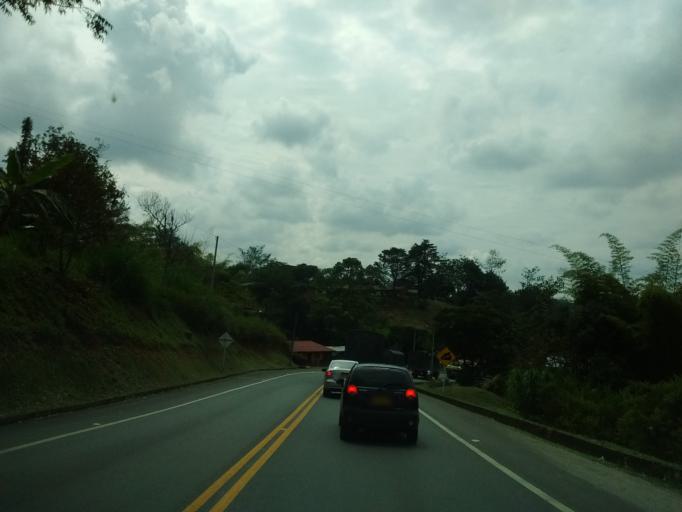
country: CO
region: Cauca
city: Caldono
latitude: 2.7986
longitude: -76.5533
